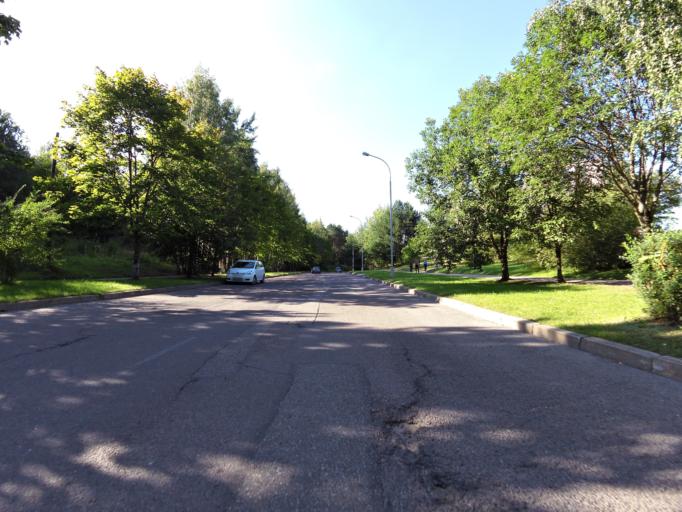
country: LT
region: Vilnius County
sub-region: Vilnius
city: Fabijoniskes
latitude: 54.7294
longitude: 25.2624
